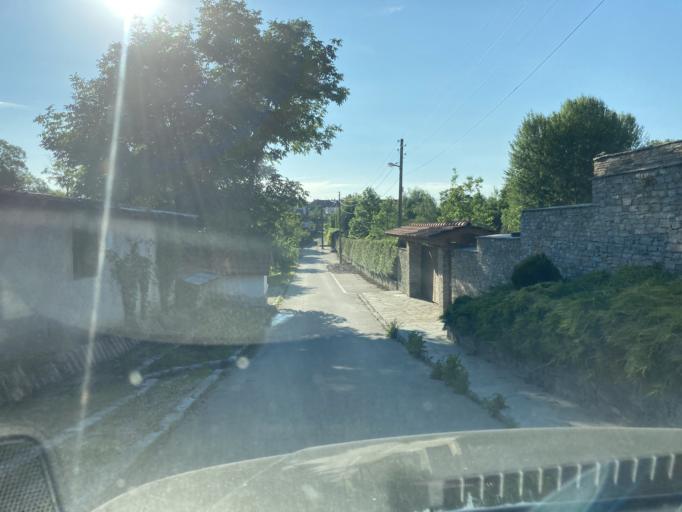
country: BG
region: Sofiya
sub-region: Obshtina Slivnitsa
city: Slivnitsa
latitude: 42.8511
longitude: 22.9835
